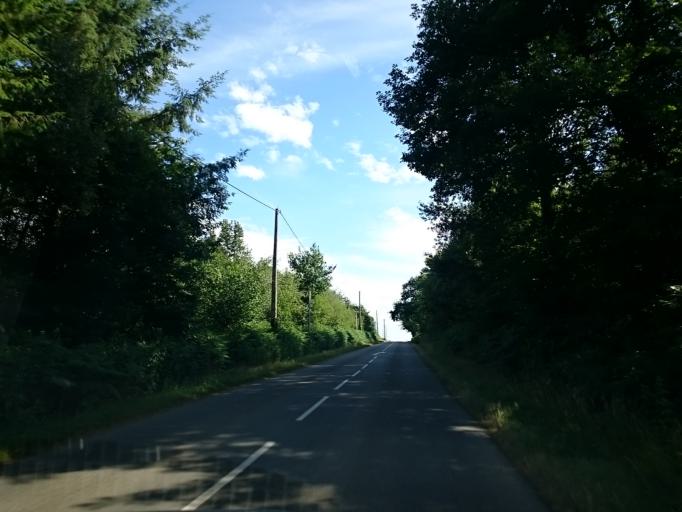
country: FR
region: Brittany
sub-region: Departement d'Ille-et-Vilaine
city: Pance
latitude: 47.9063
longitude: -1.6161
